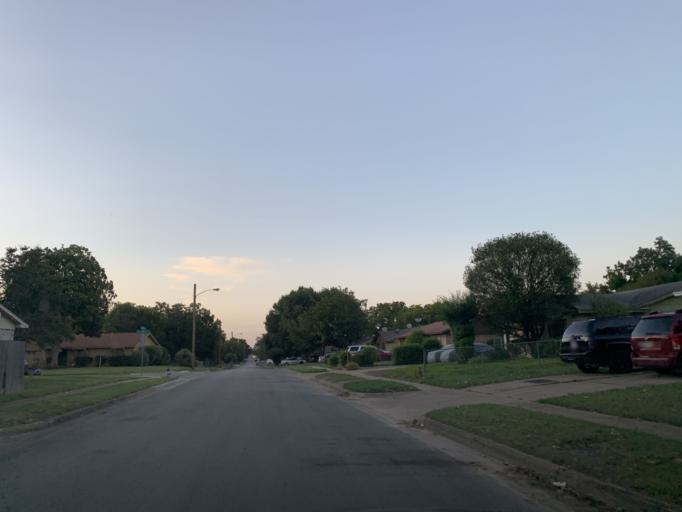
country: US
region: Texas
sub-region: Dallas County
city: Hutchins
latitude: 32.6727
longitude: -96.7932
